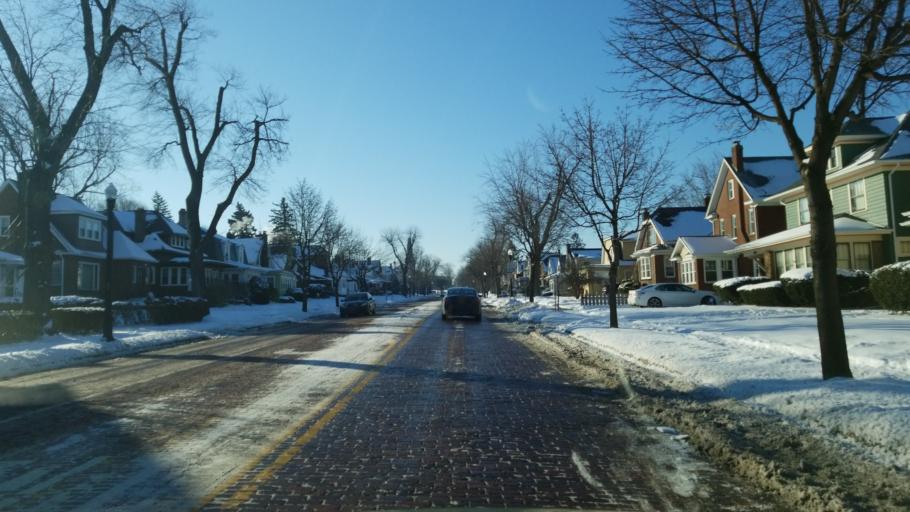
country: US
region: New York
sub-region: Erie County
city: Eggertsville
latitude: 42.9579
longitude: -78.8238
